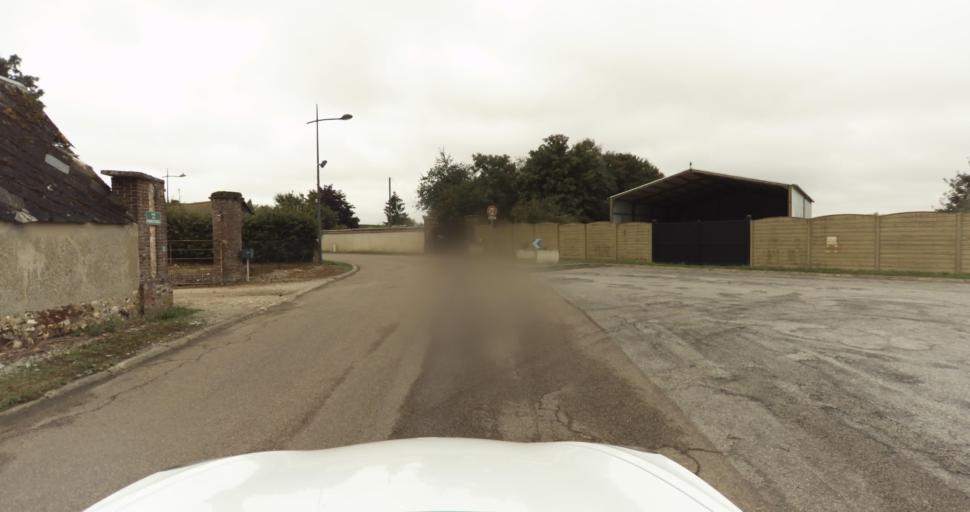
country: FR
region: Haute-Normandie
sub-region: Departement de l'Eure
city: Aviron
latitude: 49.0665
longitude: 1.0713
